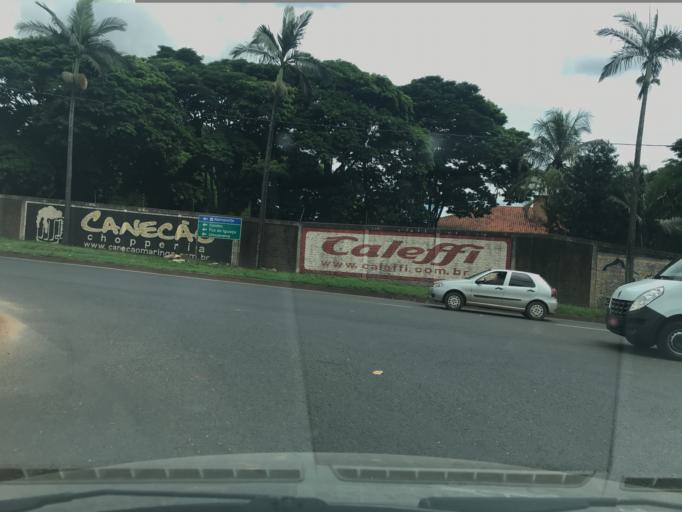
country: BR
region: Parana
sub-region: Maringa
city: Maringa
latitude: -23.4098
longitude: -51.9877
